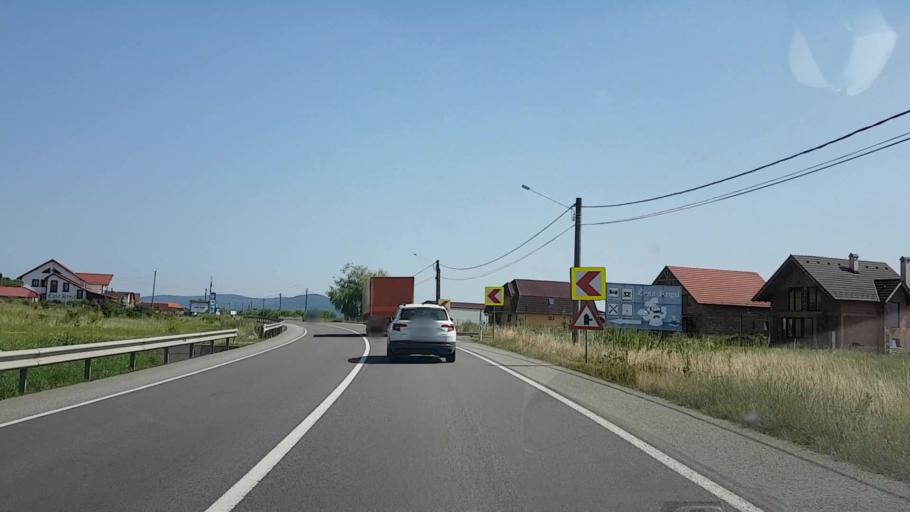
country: RO
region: Bistrita-Nasaud
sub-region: Comuna Sieu-Odorhei
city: Sieu-Odorhei
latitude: 47.1368
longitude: 24.3072
